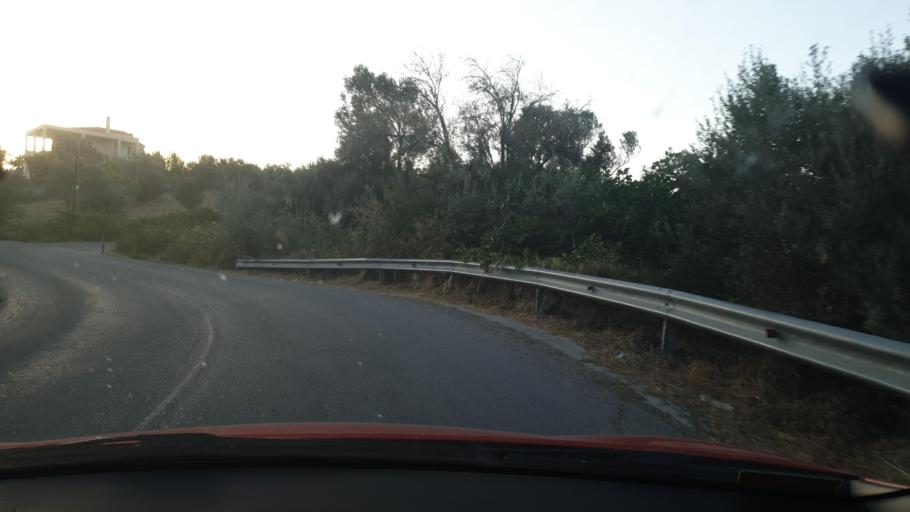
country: GR
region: Central Greece
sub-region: Nomos Evvoias
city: Oxilithos
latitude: 38.5732
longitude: 24.1193
